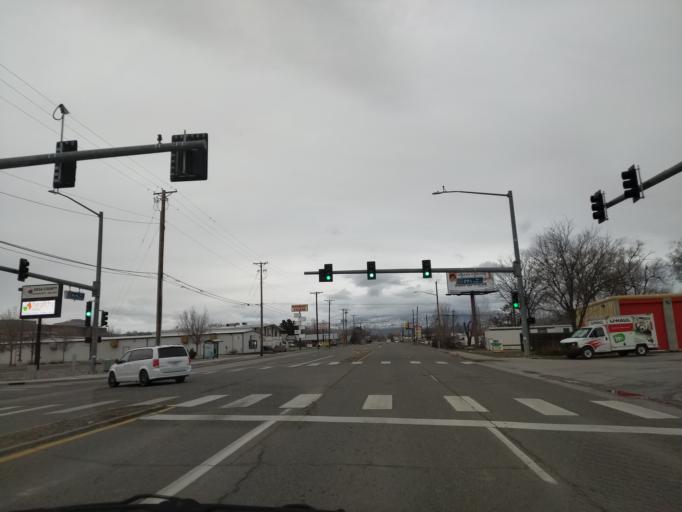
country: US
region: Colorado
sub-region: Mesa County
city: Fruitvale
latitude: 39.0773
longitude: -108.5062
